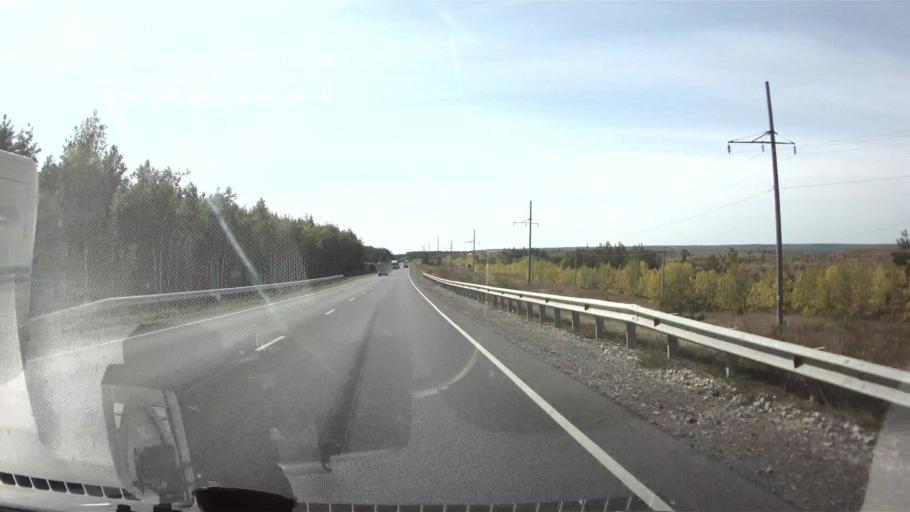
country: RU
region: Saratov
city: Khvalynsk
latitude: 52.5401
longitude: 48.0535
